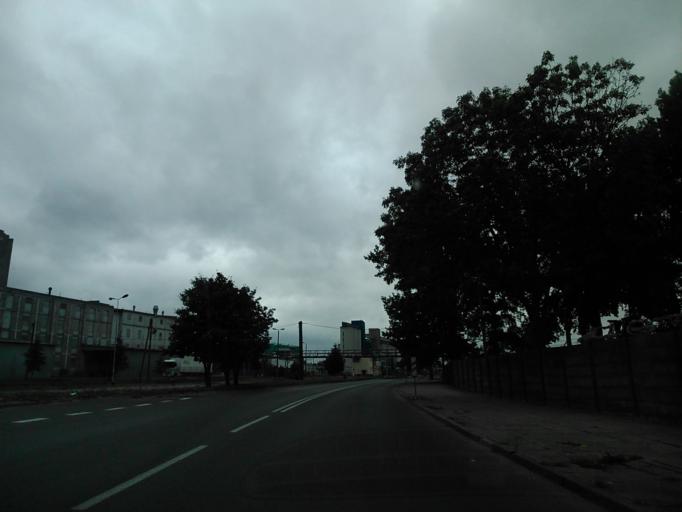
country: PL
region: Kujawsko-Pomorskie
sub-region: Powiat inowroclawski
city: Kruszwica
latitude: 52.6797
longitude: 18.3123
